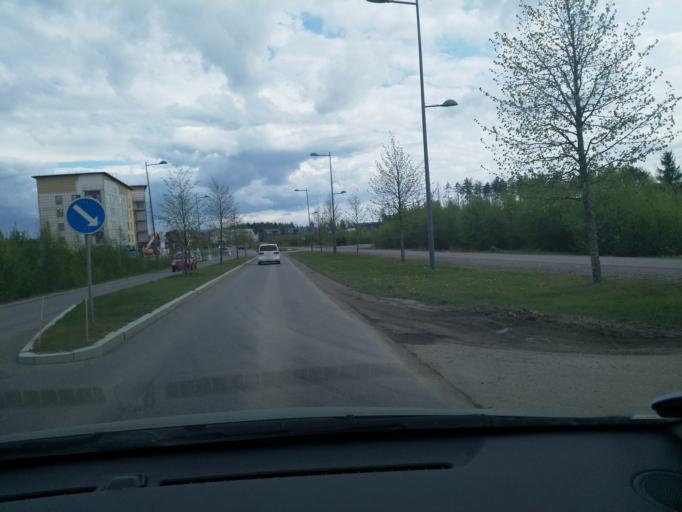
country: FI
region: Pirkanmaa
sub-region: Tampere
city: Tampere
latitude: 61.4411
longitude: 23.8081
